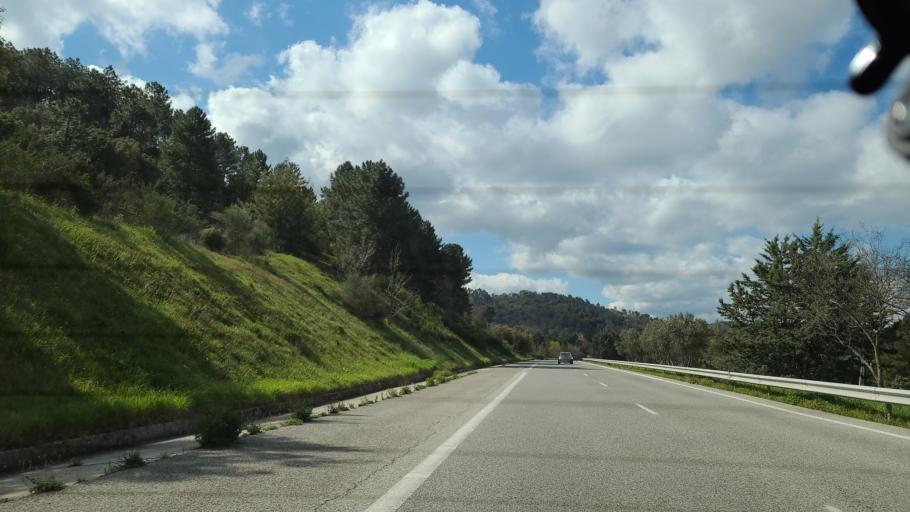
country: FR
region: Provence-Alpes-Cote d'Azur
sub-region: Departement du Var
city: Gonfaron
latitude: 43.2974
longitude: 6.2638
